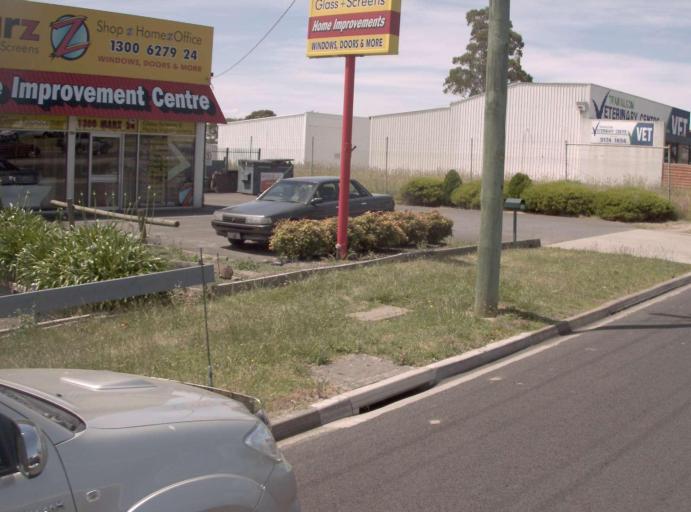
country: AU
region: Victoria
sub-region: Latrobe
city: Traralgon
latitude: -38.1915
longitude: 146.5558
